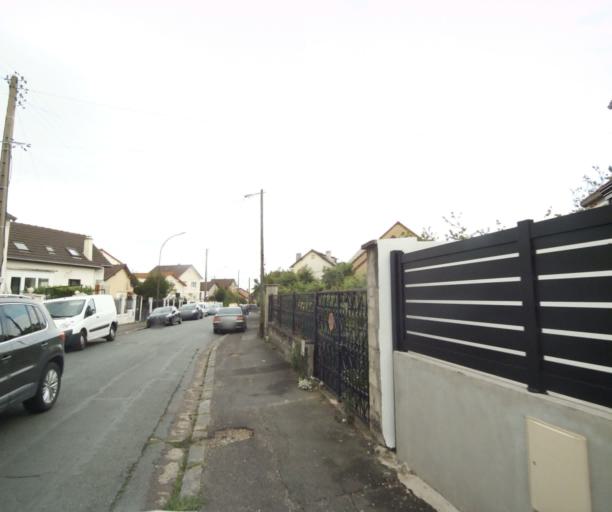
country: FR
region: Ile-de-France
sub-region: Departement du Val-d'Oise
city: Argenteuil
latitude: 48.9425
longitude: 2.2325
